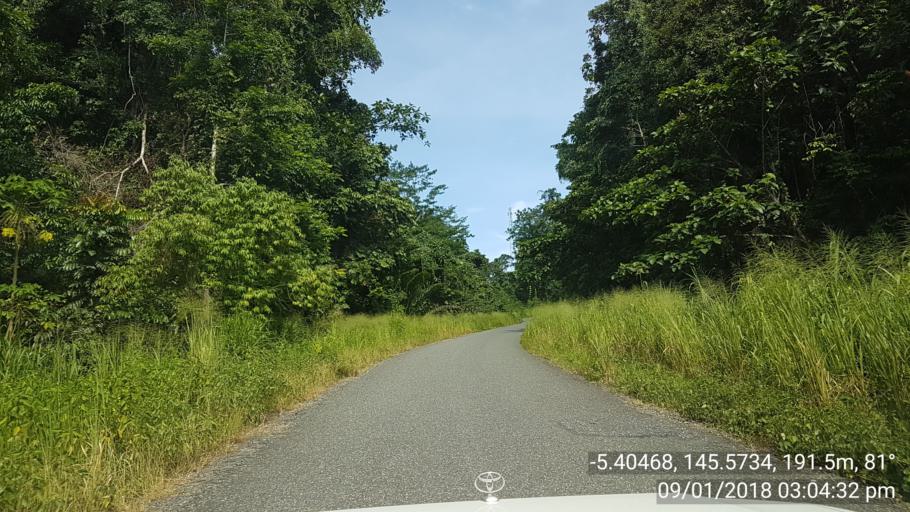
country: PG
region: Madang
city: Madang
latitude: -5.4047
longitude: 145.5733
